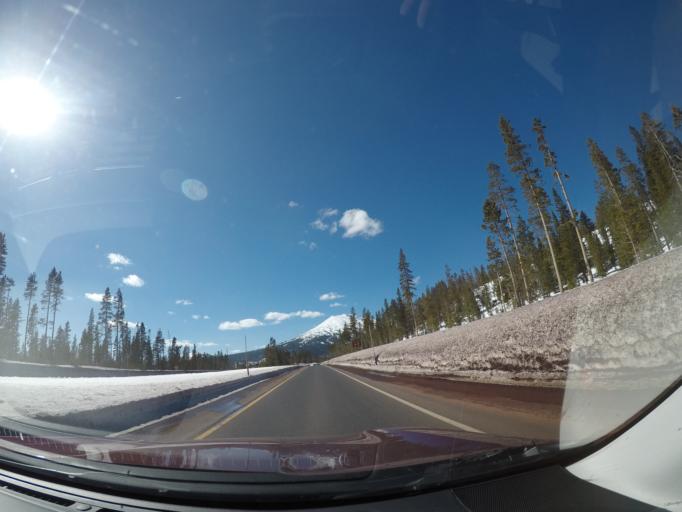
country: US
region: Oregon
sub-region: Deschutes County
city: Sunriver
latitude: 43.9831
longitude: -121.6092
